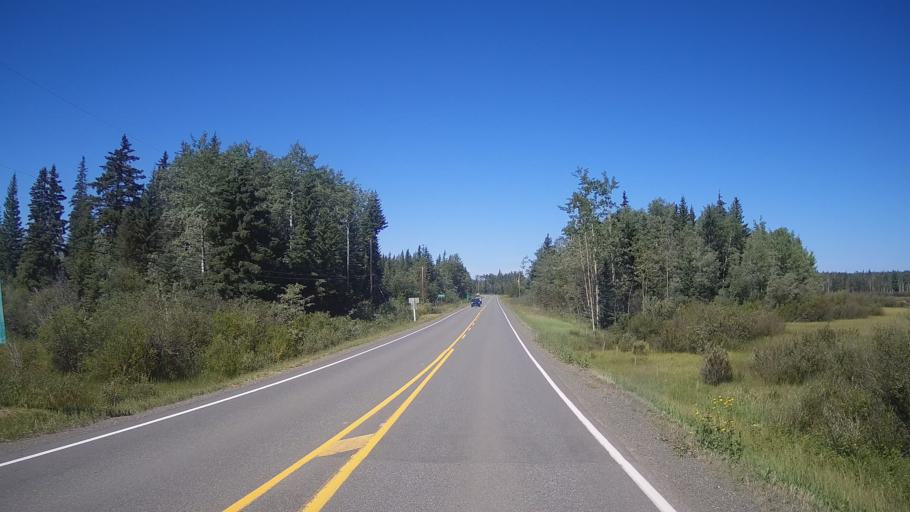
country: CA
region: British Columbia
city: Cache Creek
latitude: 51.5471
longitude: -120.9183
